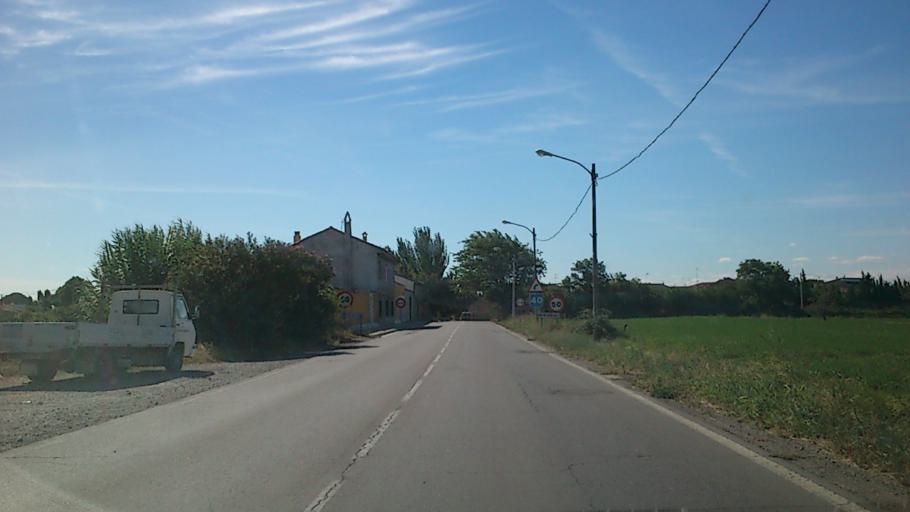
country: ES
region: Aragon
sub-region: Provincia de Zaragoza
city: Villanueva de Gallego
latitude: 41.6977
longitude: -0.8161
